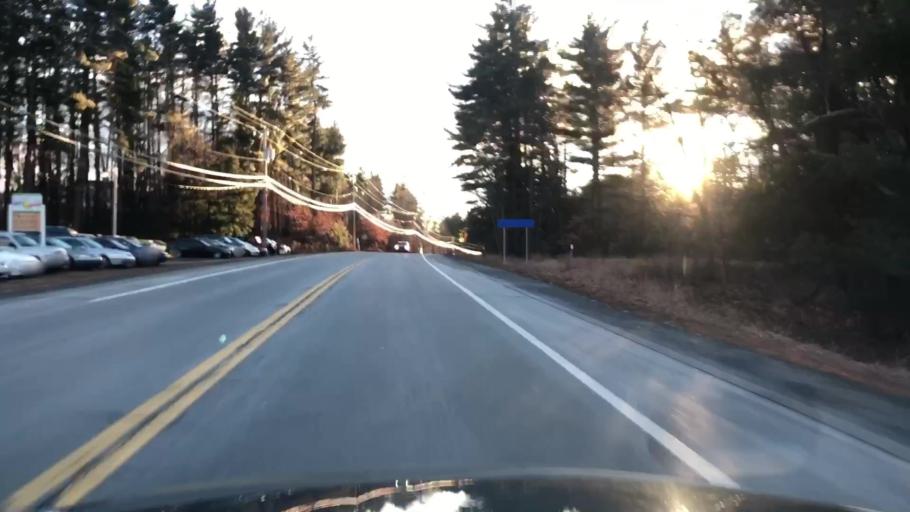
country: US
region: New Hampshire
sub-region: Hillsborough County
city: Brookline
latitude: 42.7112
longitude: -71.6655
